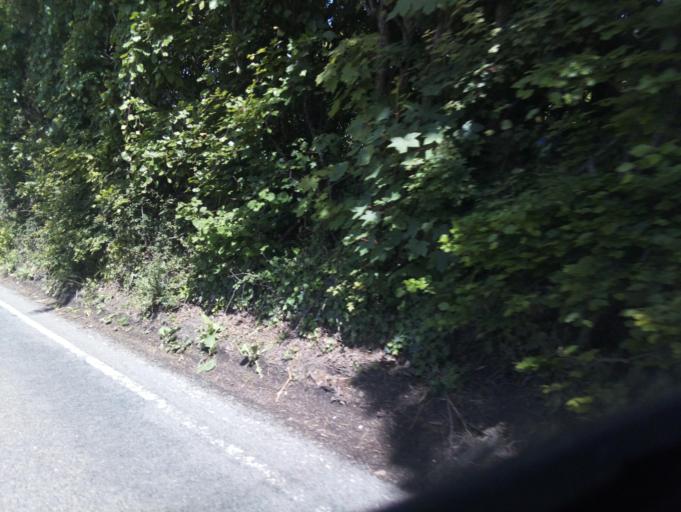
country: GB
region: England
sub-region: Devon
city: Ottery St Mary
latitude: 50.8198
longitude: -3.2673
